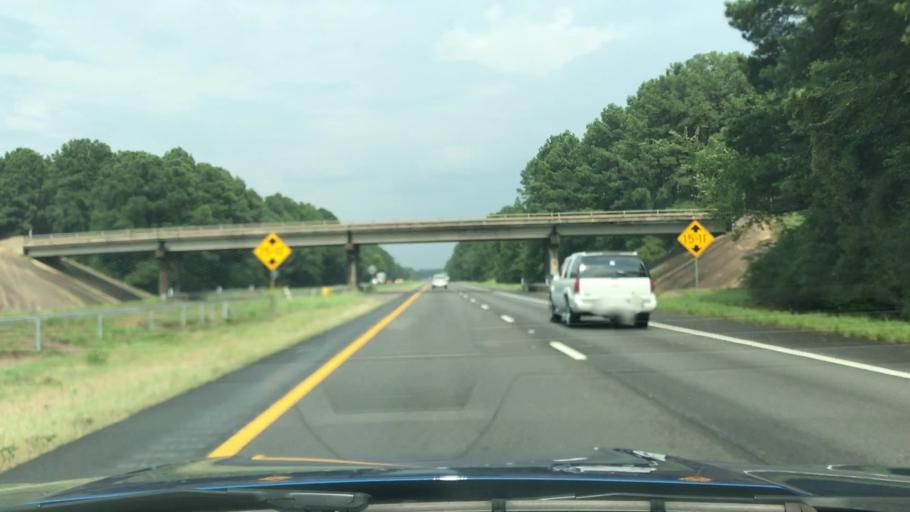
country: US
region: Texas
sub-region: Harrison County
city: Hallsville
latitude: 32.4801
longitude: -94.5455
